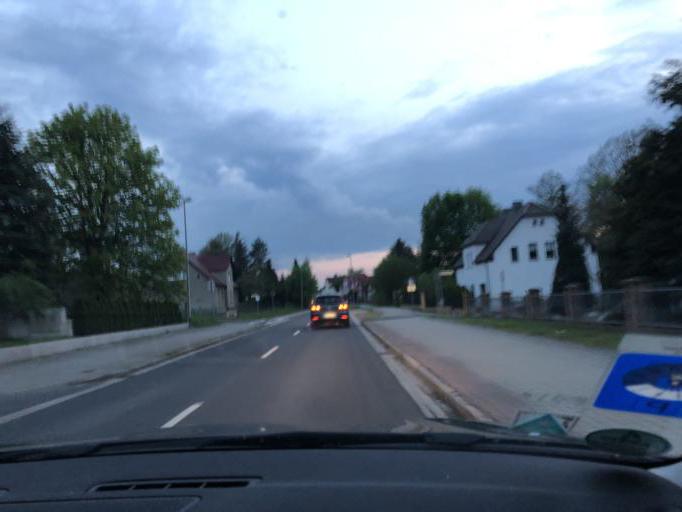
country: DE
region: Saxony
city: Krauschwitz
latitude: 51.5186
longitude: 14.7203
